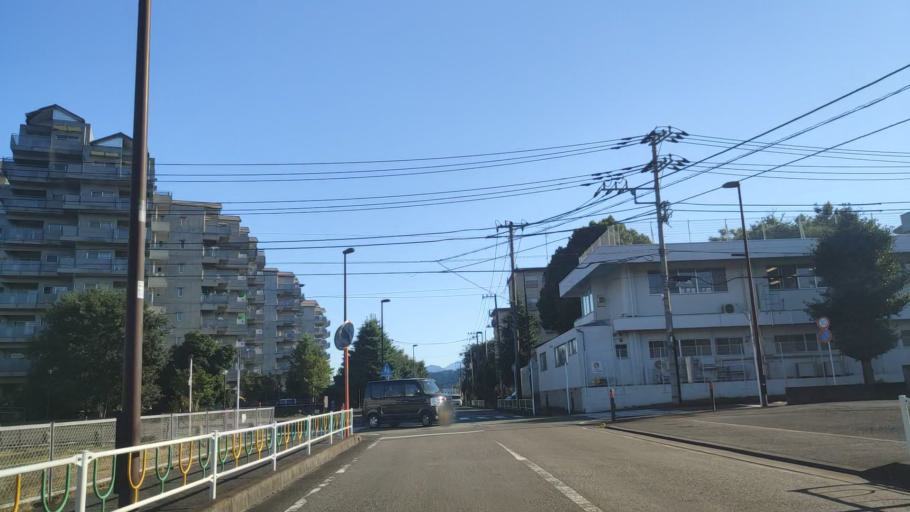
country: JP
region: Tokyo
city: Hachioji
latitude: 35.5868
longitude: 139.3148
